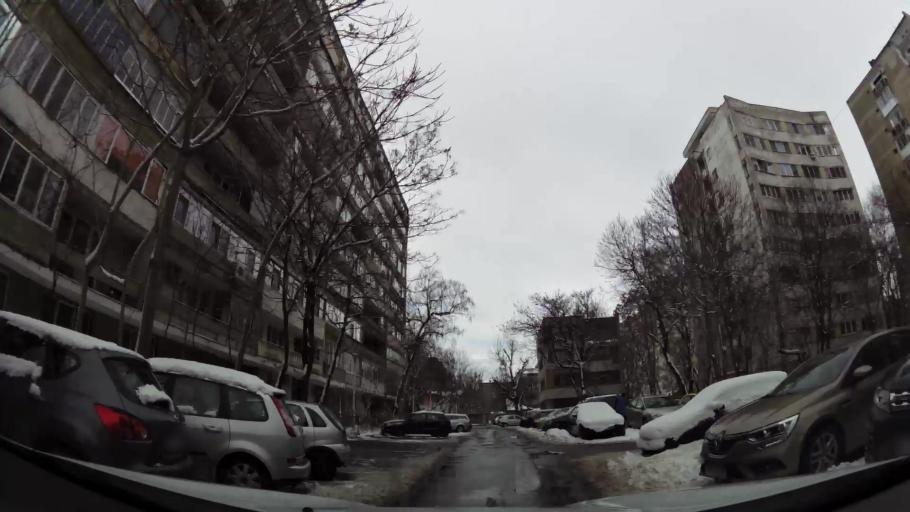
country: RO
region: Bucuresti
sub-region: Municipiul Bucuresti
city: Bucharest
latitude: 44.3946
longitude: 26.1178
